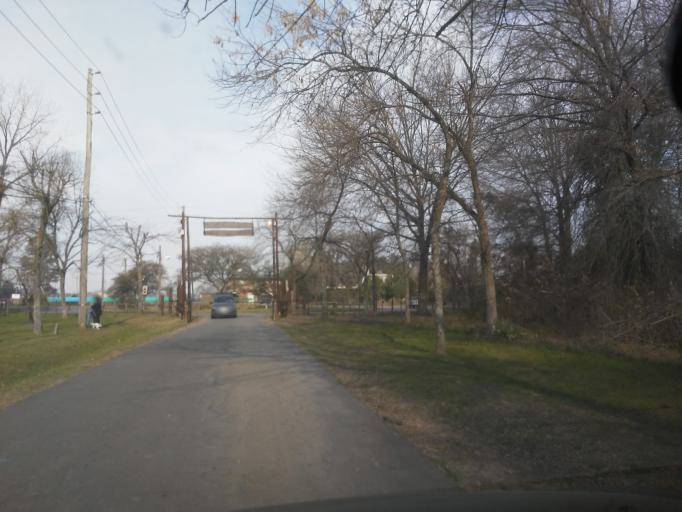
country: AR
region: Buenos Aires
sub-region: Partido de Marcos Paz
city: Marcos Paz
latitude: -34.6699
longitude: -58.8564
